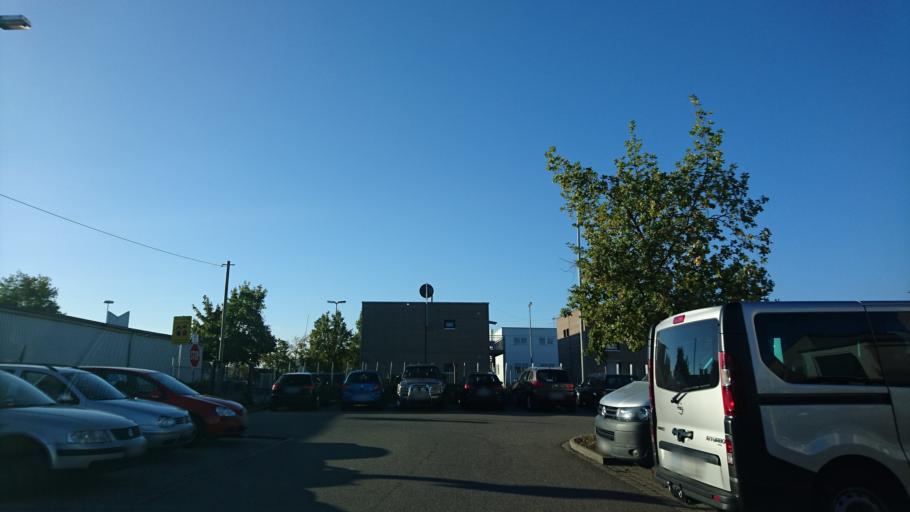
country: DE
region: Bavaria
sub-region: Swabia
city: Gersthofen
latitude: 48.4131
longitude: 10.8754
